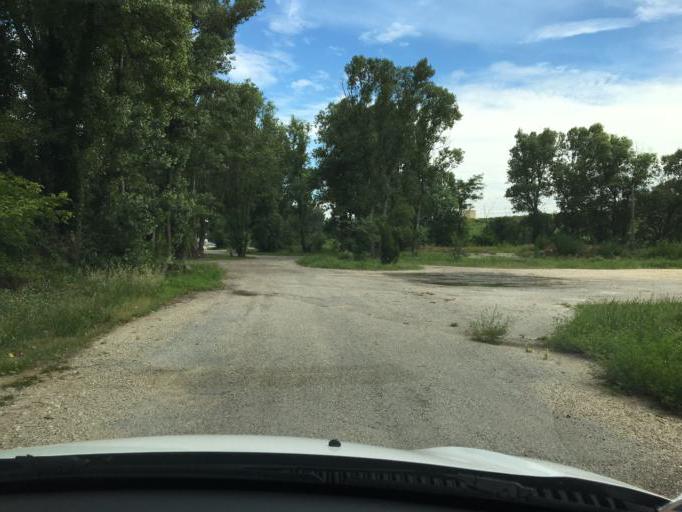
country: FR
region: Provence-Alpes-Cote d'Azur
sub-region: Departement du Vaucluse
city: Bollene
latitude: 44.3080
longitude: 4.7349
